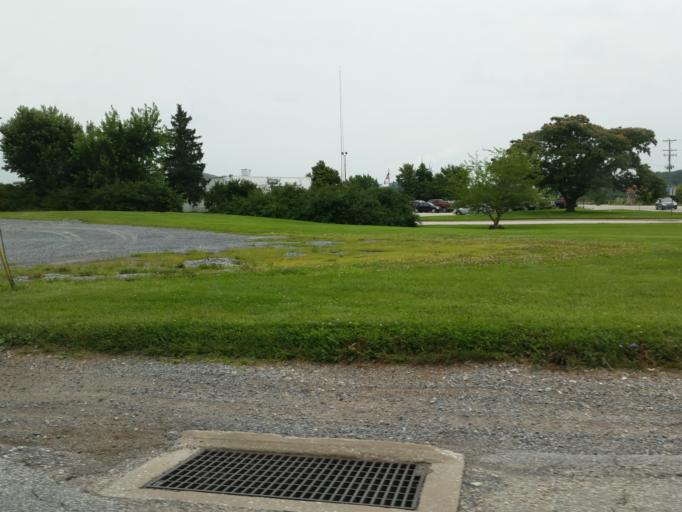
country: US
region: Pennsylvania
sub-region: York County
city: Emigsville
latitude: 40.0198
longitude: -76.7475
